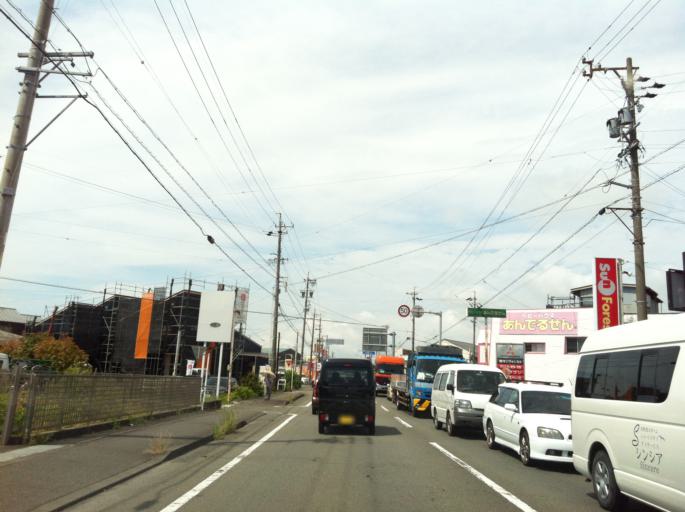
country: JP
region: Shizuoka
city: Yaizu
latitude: 34.8293
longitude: 138.3002
